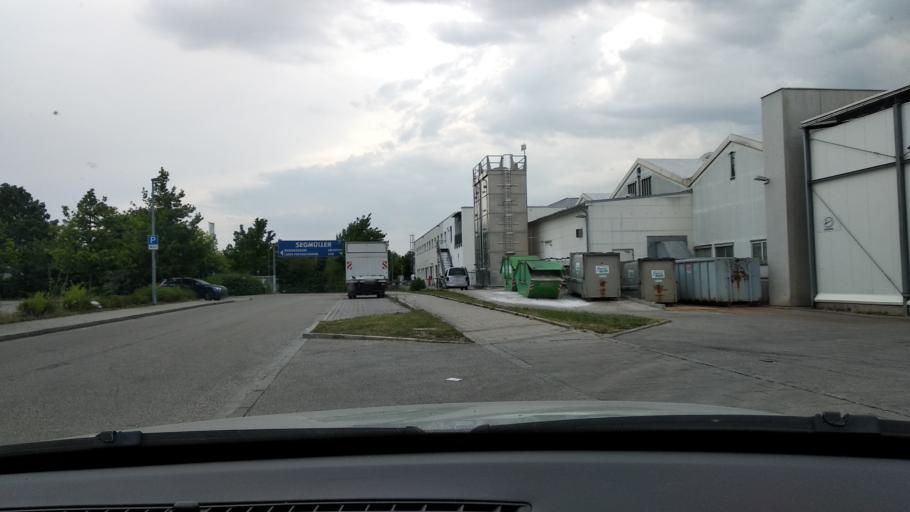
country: DE
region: Bavaria
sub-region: Upper Bavaria
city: Kirchheim bei Muenchen
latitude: 48.1455
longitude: 11.7822
